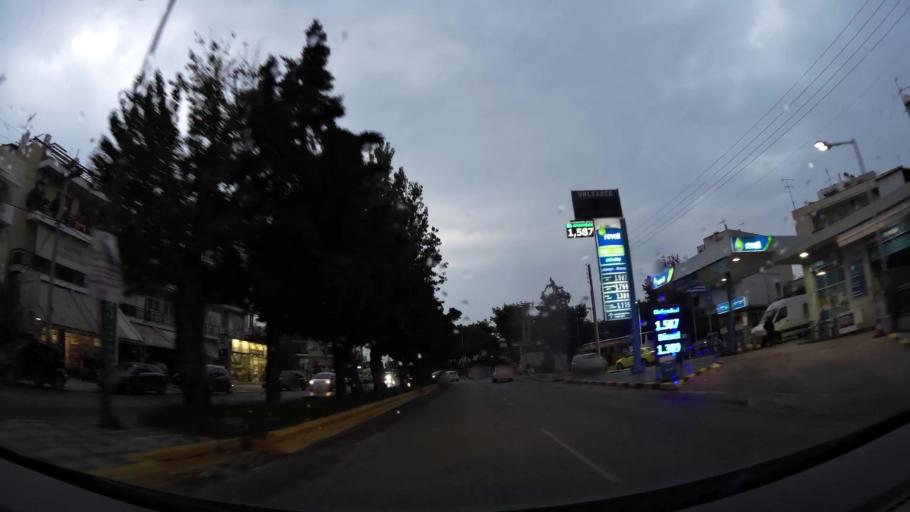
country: GR
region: Attica
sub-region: Nomarchia Athinas
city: Ymittos
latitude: 37.9456
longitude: 23.7476
